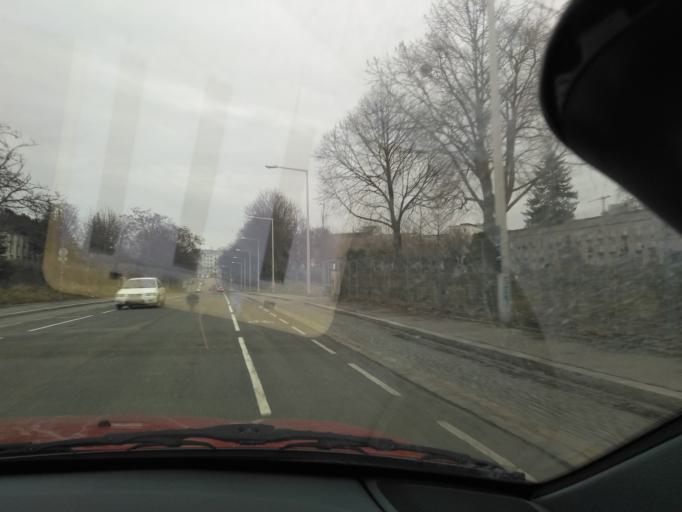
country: AT
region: Vienna
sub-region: Wien Stadt
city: Vienna
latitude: 48.1741
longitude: 16.3399
